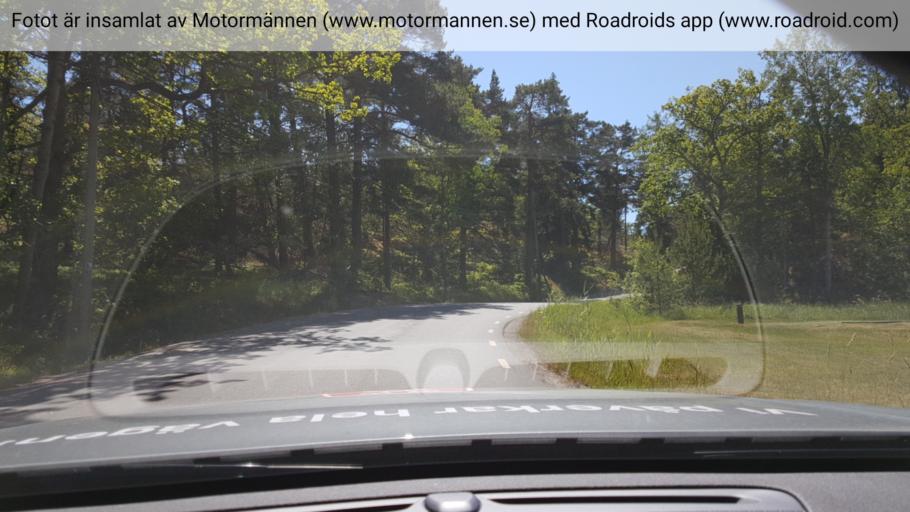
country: SE
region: Stockholm
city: Dalaro
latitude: 59.1631
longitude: 18.4488
